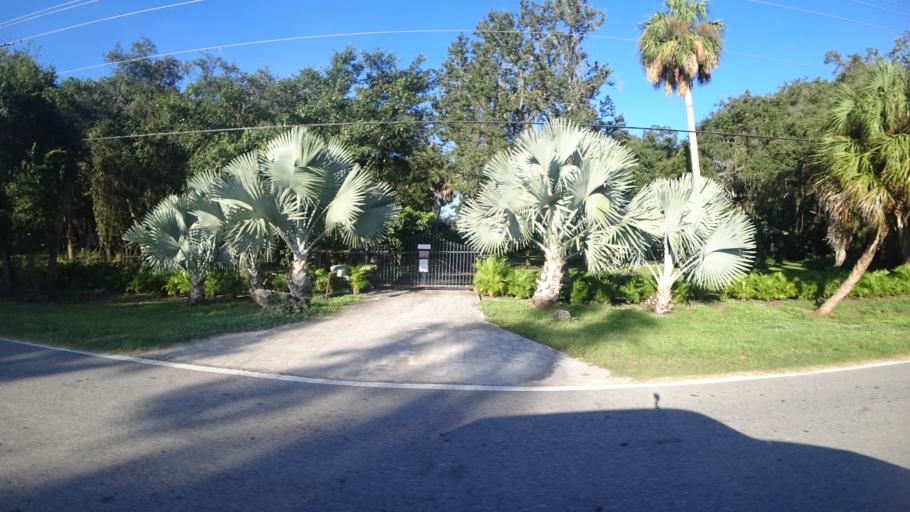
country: US
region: Florida
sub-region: Manatee County
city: Memphis
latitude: 27.5706
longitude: -82.5565
